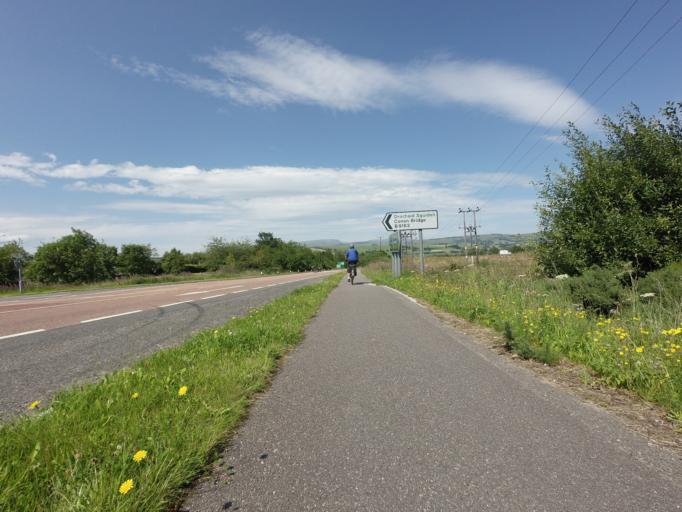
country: GB
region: Scotland
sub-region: Highland
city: Conon Bridge
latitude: 57.5666
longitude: -4.4238
